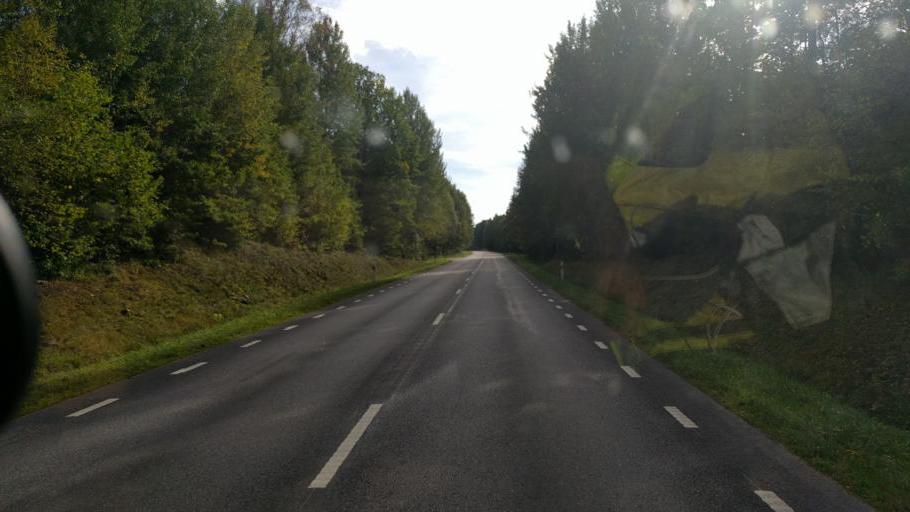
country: SE
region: OEstergoetland
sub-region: Kinda Kommun
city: Kisa
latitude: 57.9429
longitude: 15.6670
